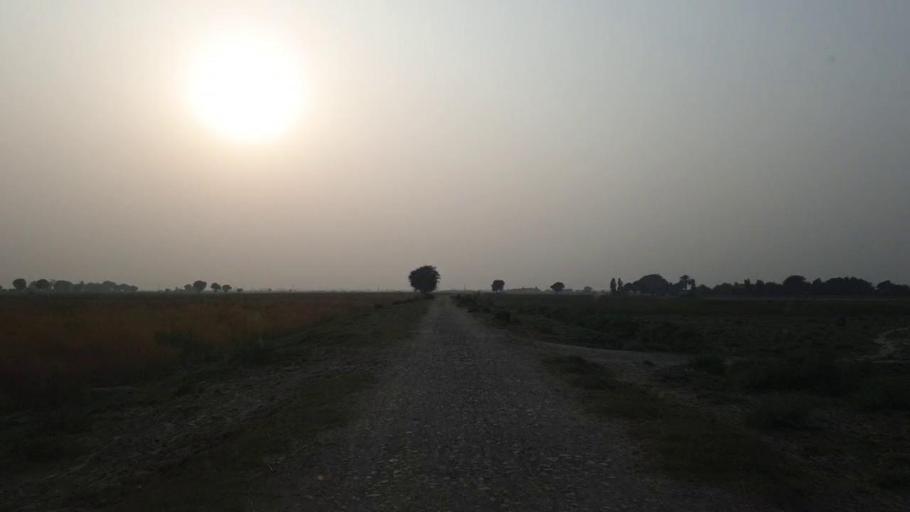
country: PK
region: Sindh
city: Mirpur Batoro
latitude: 24.6633
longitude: 68.3829
